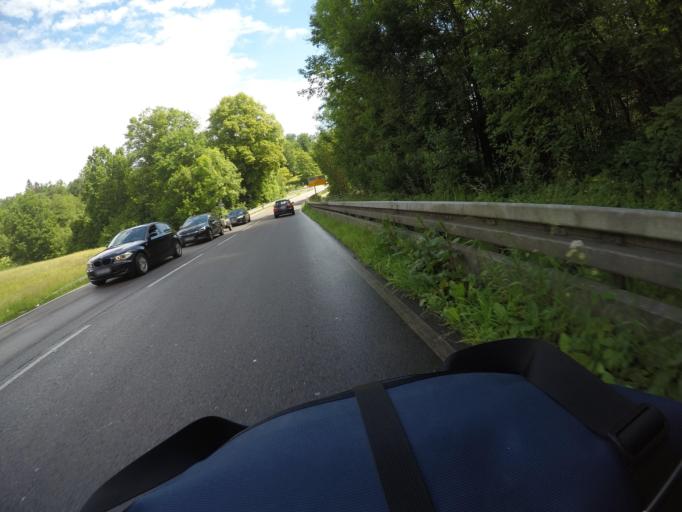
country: DE
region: Baden-Wuerttemberg
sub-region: Regierungsbezirk Stuttgart
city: Gerlingen
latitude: 48.7549
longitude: 9.0904
